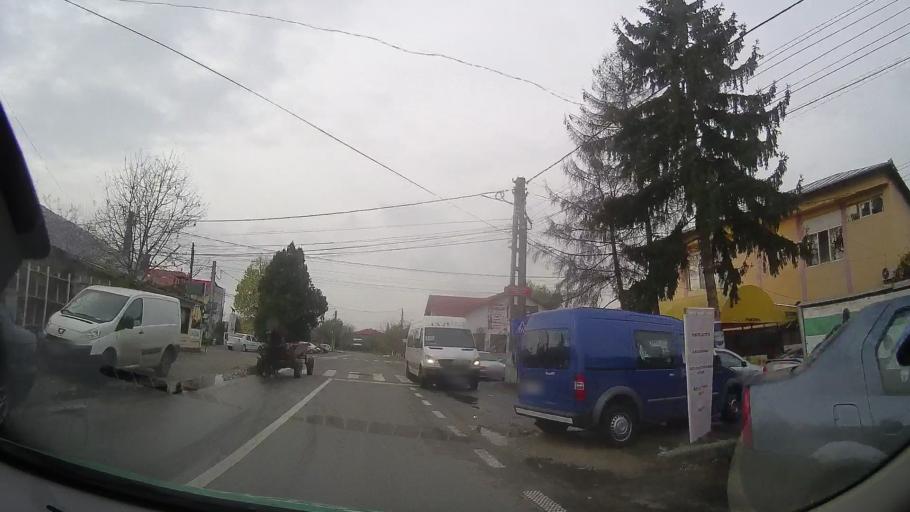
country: RO
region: Ilfov
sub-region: Comuna Gruiu
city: Gruiu
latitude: 44.7252
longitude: 26.2277
